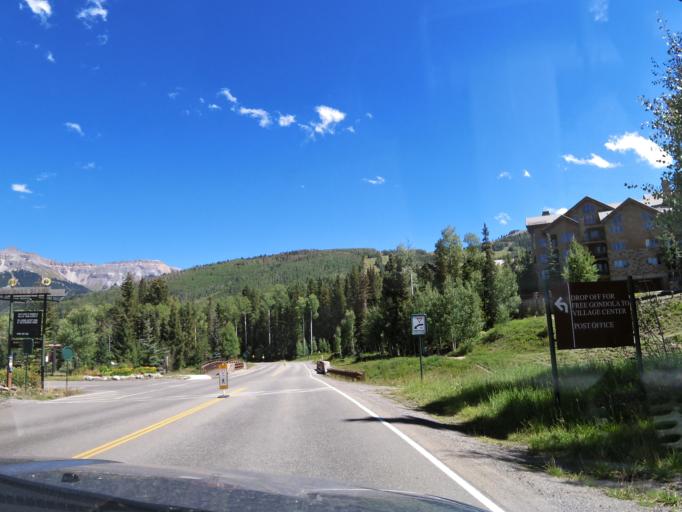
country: US
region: Colorado
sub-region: San Miguel County
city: Mountain Village
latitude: 37.9318
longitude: -107.8539
